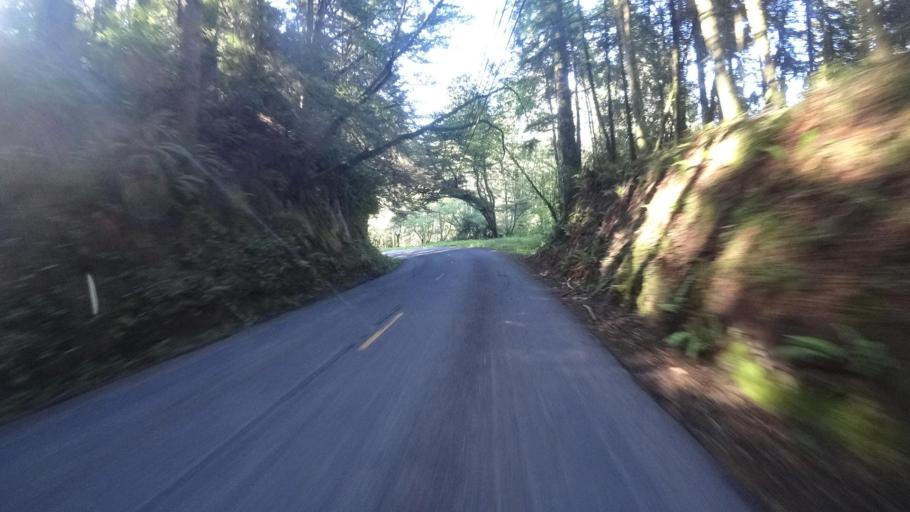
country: US
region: California
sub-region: Humboldt County
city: McKinleyville
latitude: 40.9856
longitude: -124.1004
